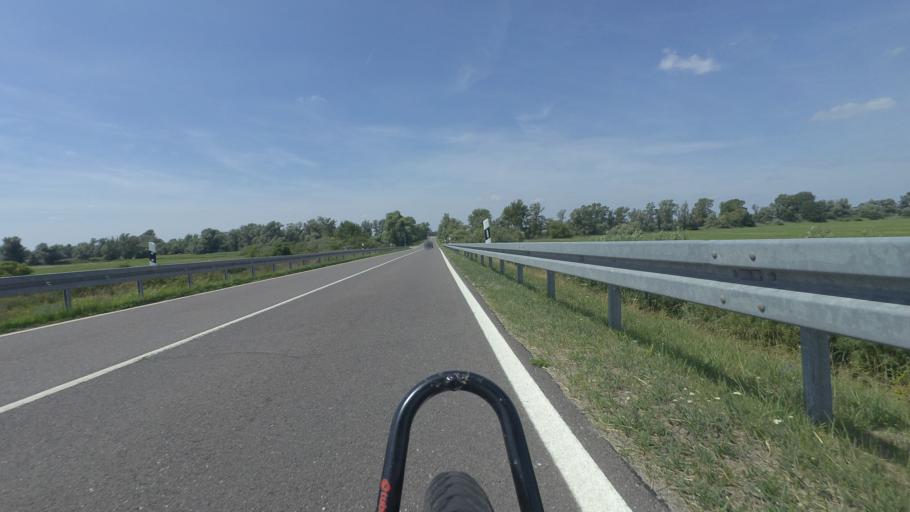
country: DE
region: Saxony-Anhalt
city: Schollene
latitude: 52.7691
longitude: 12.2189
